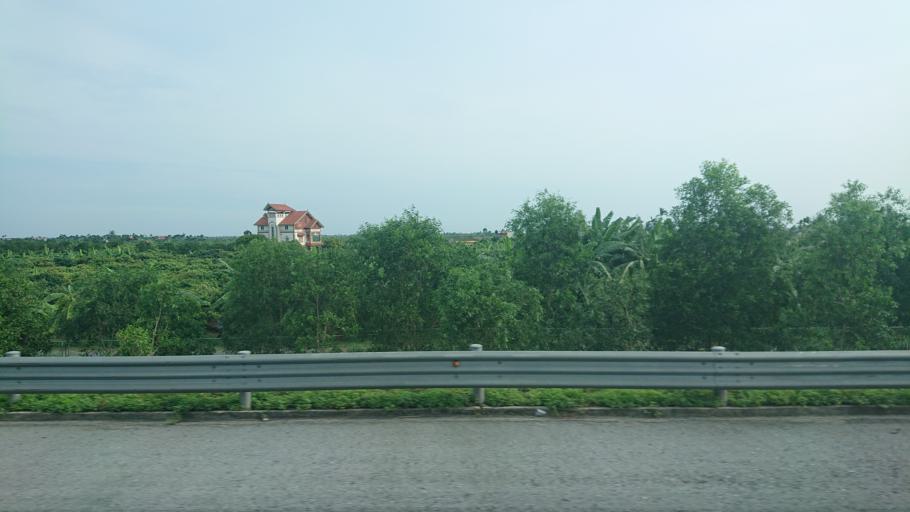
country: VN
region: Hai Duong
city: Tu Ky
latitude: 20.8202
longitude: 106.4786
